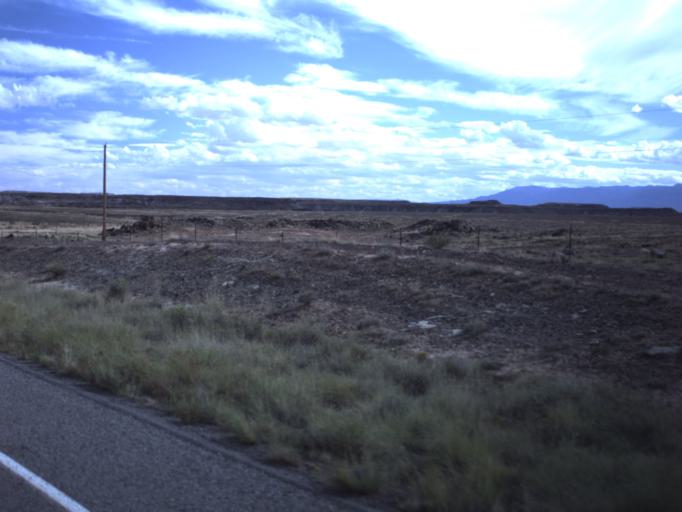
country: US
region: Colorado
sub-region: Montezuma County
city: Towaoc
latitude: 37.1636
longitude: -109.0719
